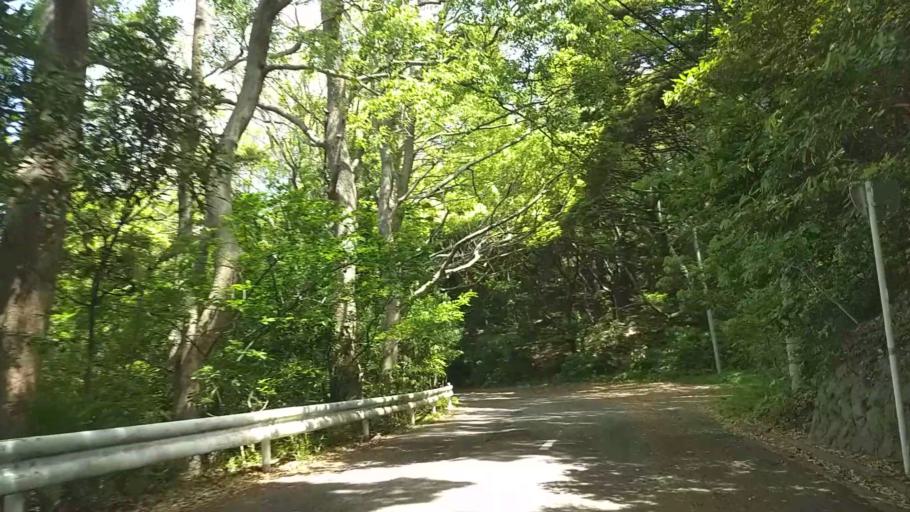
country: JP
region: Kanagawa
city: Yugawara
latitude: 35.1421
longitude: 139.1528
